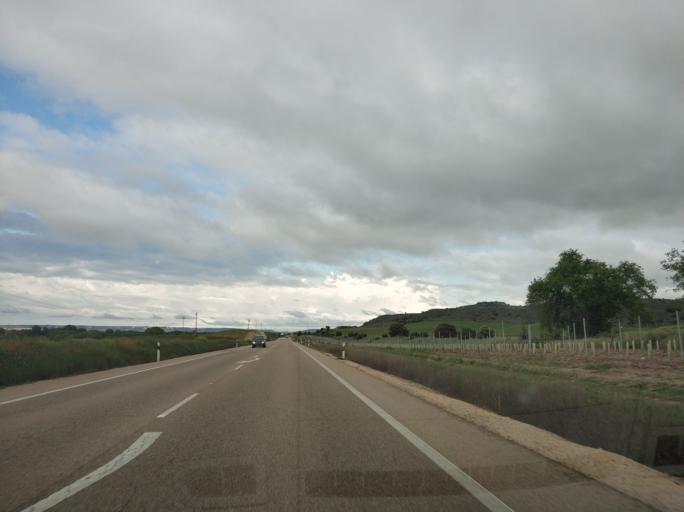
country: ES
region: Castille and Leon
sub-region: Provincia de Valladolid
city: Valbuena de Duero
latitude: 41.6241
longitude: -4.2679
